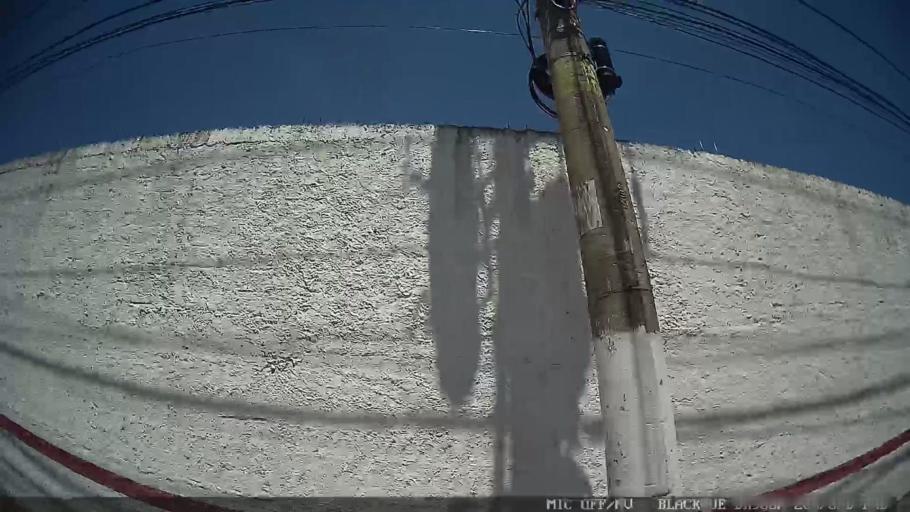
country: BR
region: Sao Paulo
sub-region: Sao Caetano Do Sul
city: Sao Caetano do Sul
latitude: -23.6003
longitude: -46.5495
